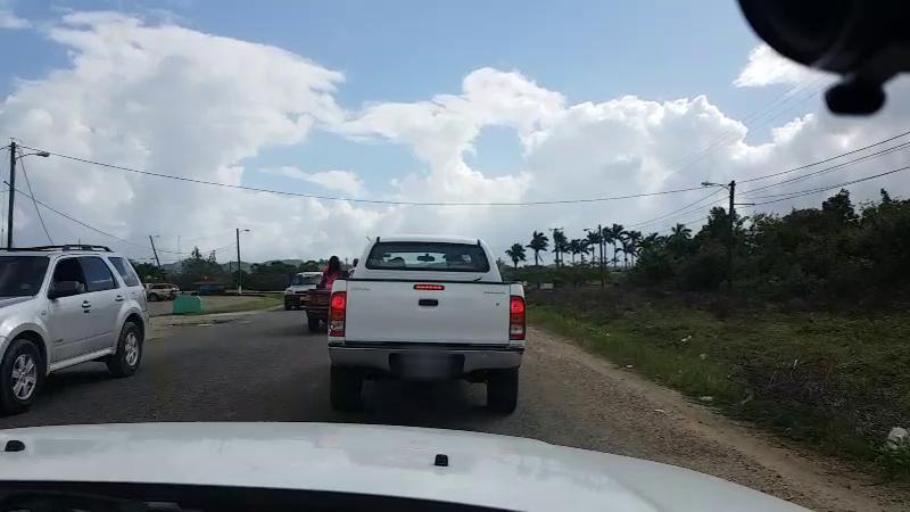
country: BZ
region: Cayo
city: Belmopan
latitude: 17.2420
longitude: -88.7825
